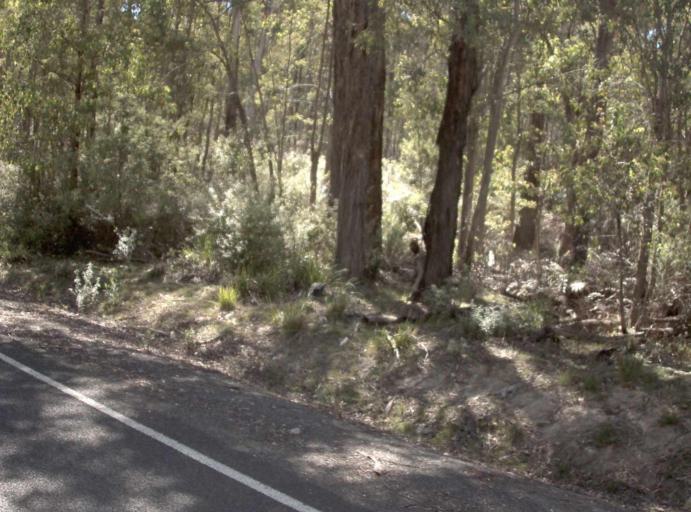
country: AU
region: New South Wales
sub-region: Bombala
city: Bombala
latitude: -37.1363
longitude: 148.7398
